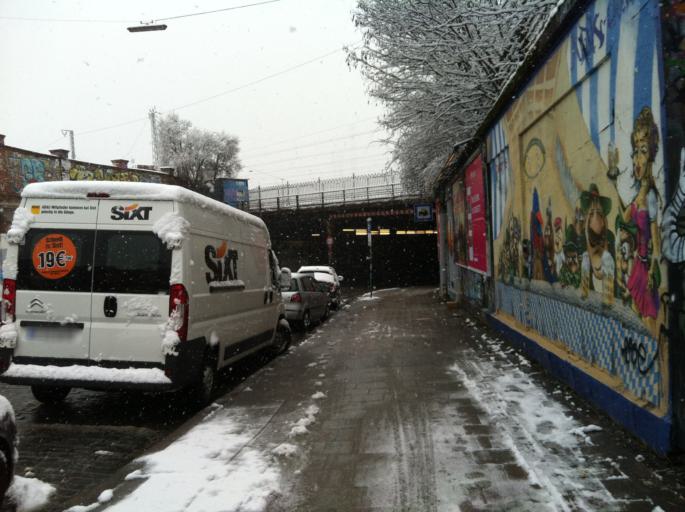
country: DE
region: Bavaria
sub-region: Upper Bavaria
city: Munich
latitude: 48.1223
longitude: 11.5544
